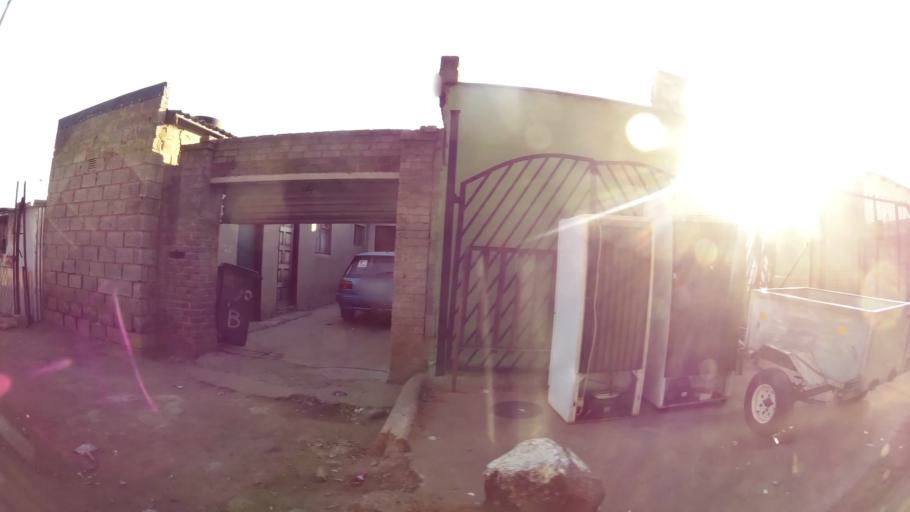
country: ZA
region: Gauteng
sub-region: City of Johannesburg Metropolitan Municipality
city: Soweto
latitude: -26.2554
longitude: 27.8785
